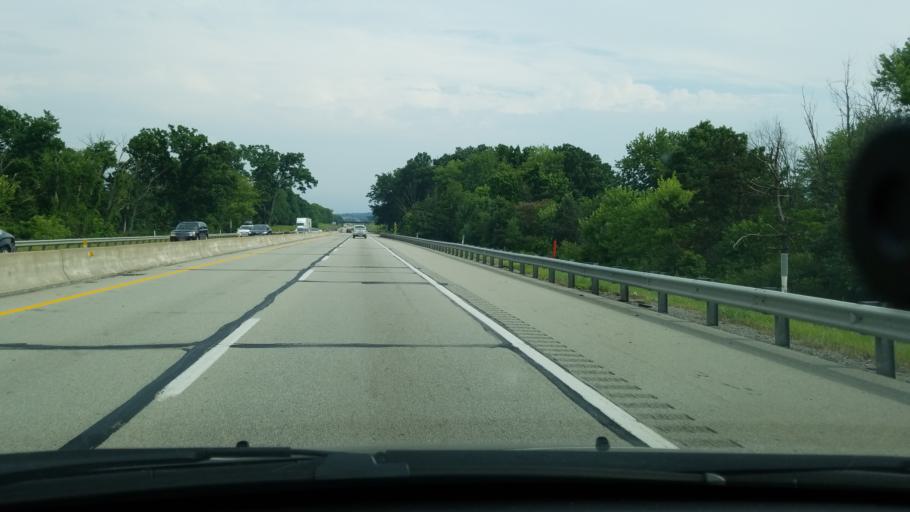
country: US
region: Pennsylvania
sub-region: Butler County
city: Cranberry Township
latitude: 40.6911
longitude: -80.1125
